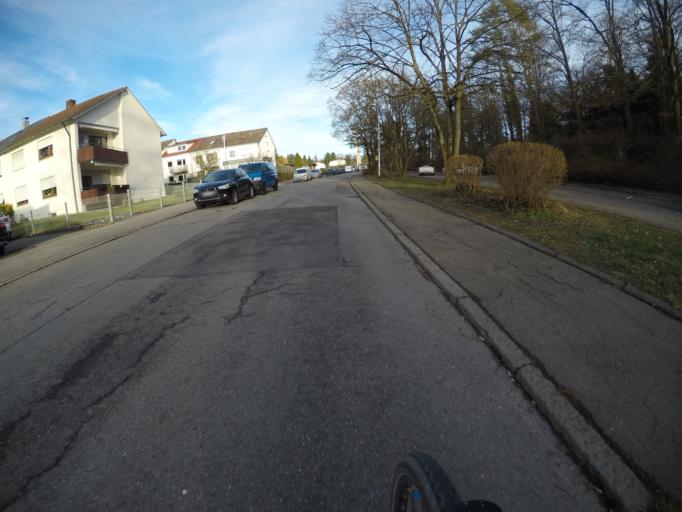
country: DE
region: Baden-Wuerttemberg
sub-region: Regierungsbezirk Stuttgart
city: Boeblingen
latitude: 48.6847
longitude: 9.0215
